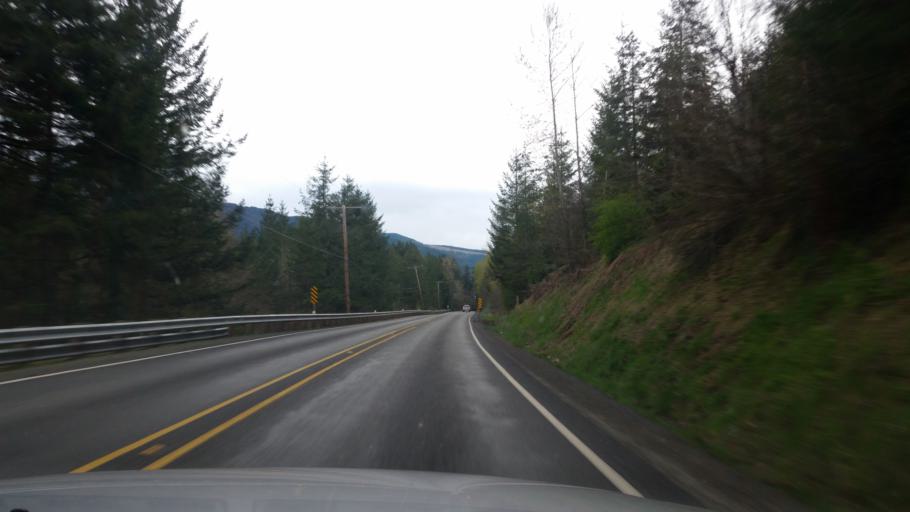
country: US
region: Washington
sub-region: Pierce County
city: Eatonville
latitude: 46.8051
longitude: -122.2677
